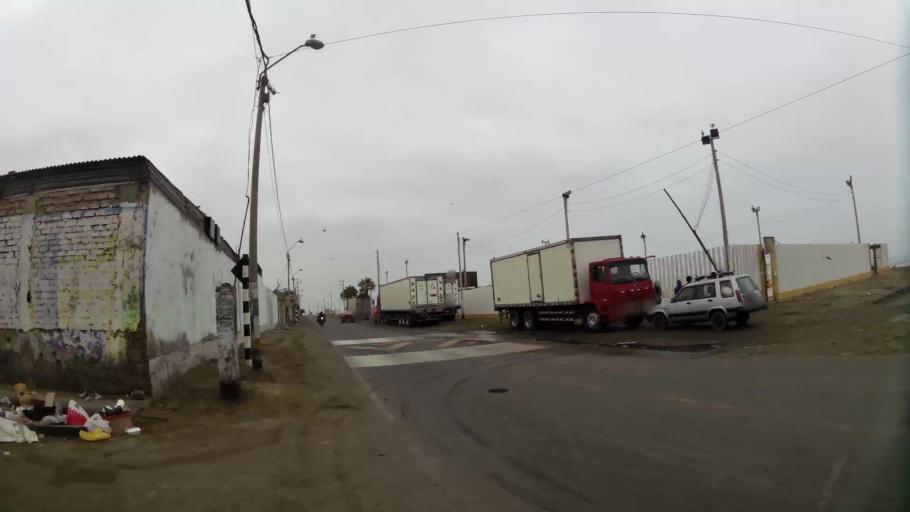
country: PE
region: Ica
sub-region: Provincia de Pisco
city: Pisco
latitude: -13.7344
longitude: -76.2247
